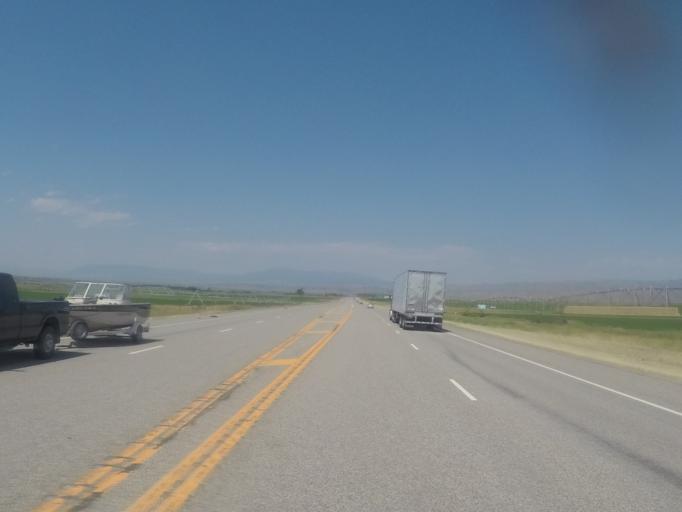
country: US
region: Montana
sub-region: Broadwater County
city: Townsend
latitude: 46.1189
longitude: -111.4993
